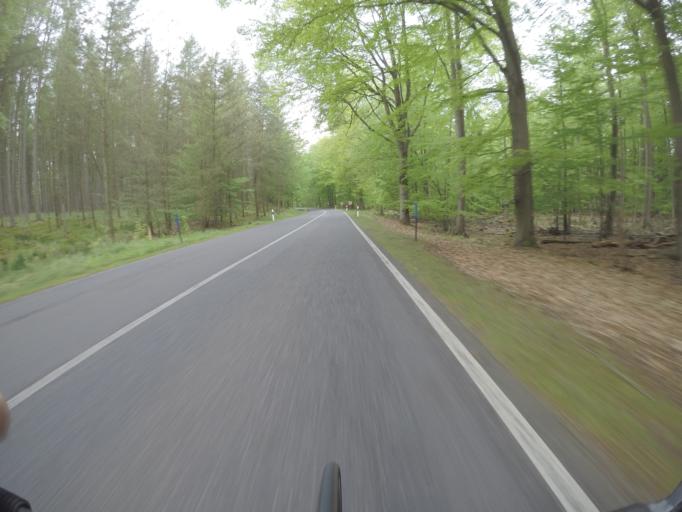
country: DE
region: Brandenburg
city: Joachimsthal
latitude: 52.9347
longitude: 13.7346
